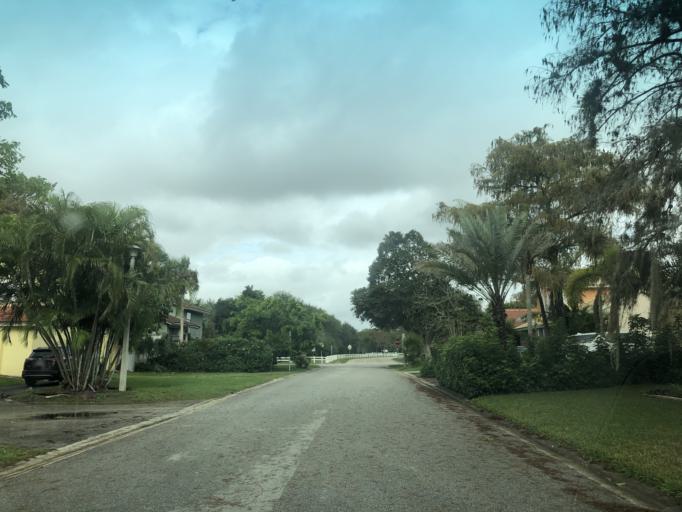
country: US
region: Florida
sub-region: Broward County
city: Coral Springs
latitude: 26.2474
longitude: -80.2471
